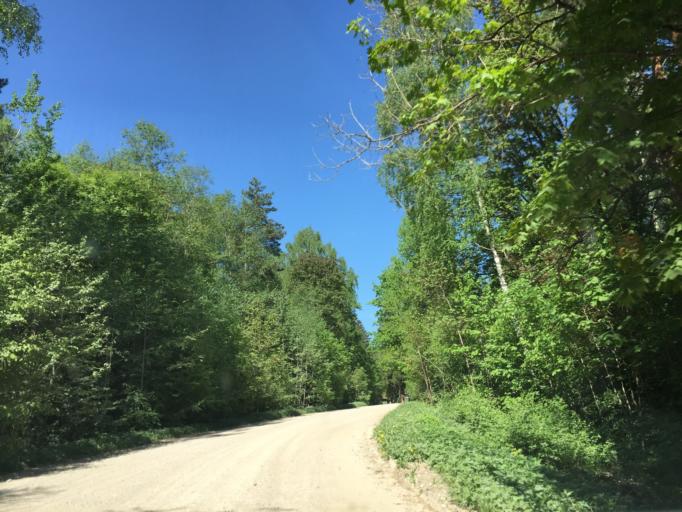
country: LV
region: Ikskile
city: Ikskile
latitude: 56.8547
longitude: 24.5091
